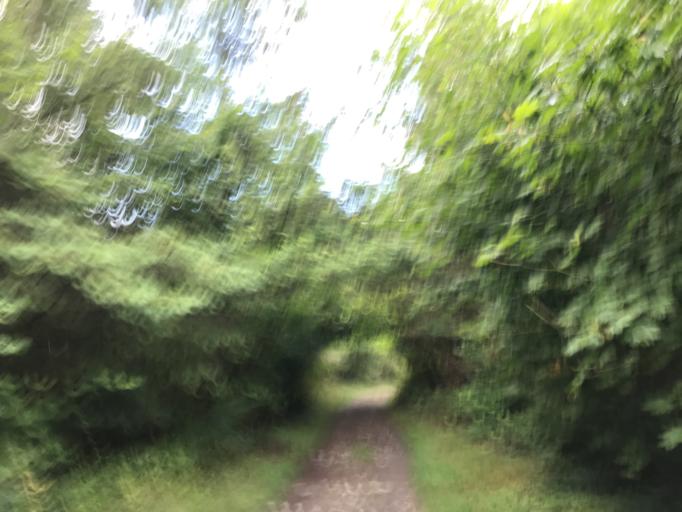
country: US
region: Washington
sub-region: King County
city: Ravensdale
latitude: 47.3409
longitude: -122.0058
